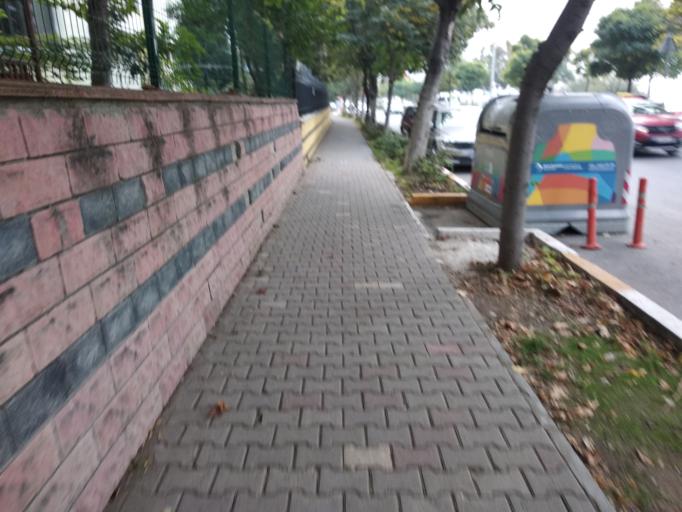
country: TR
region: Istanbul
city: Beylikduezue
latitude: 41.0028
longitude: 28.6390
